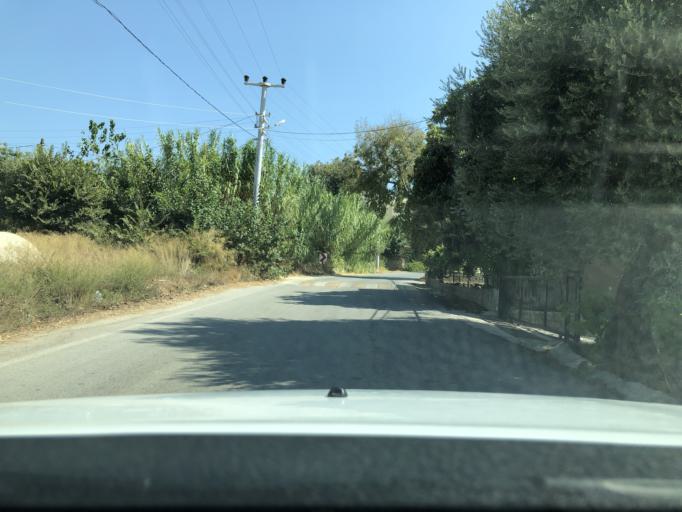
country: TR
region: Antalya
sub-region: Manavgat
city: Manavgat
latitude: 36.8124
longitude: 31.4879
